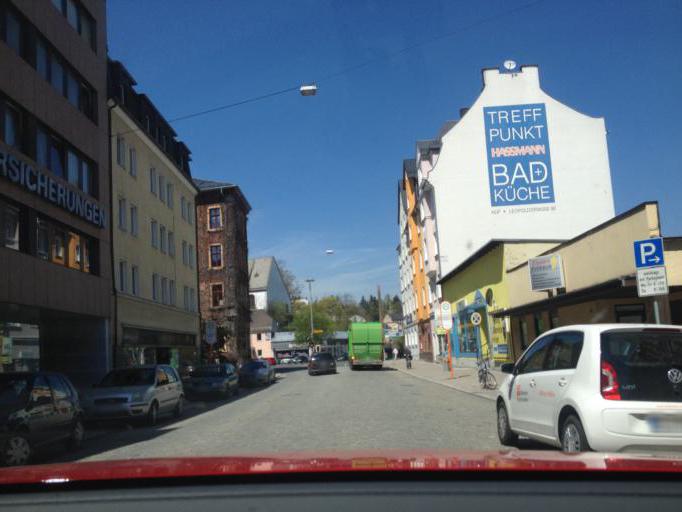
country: DE
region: Bavaria
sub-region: Upper Franconia
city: Hof
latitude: 50.3133
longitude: 11.9196
